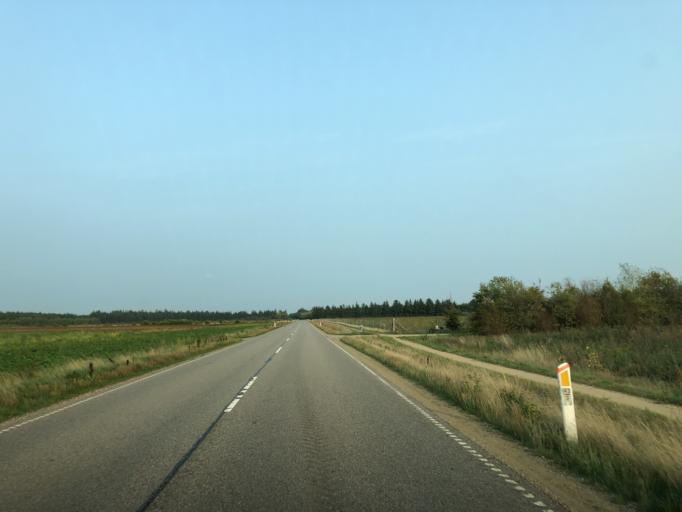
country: DK
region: South Denmark
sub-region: Billund Kommune
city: Grindsted
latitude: 55.8325
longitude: 8.9490
